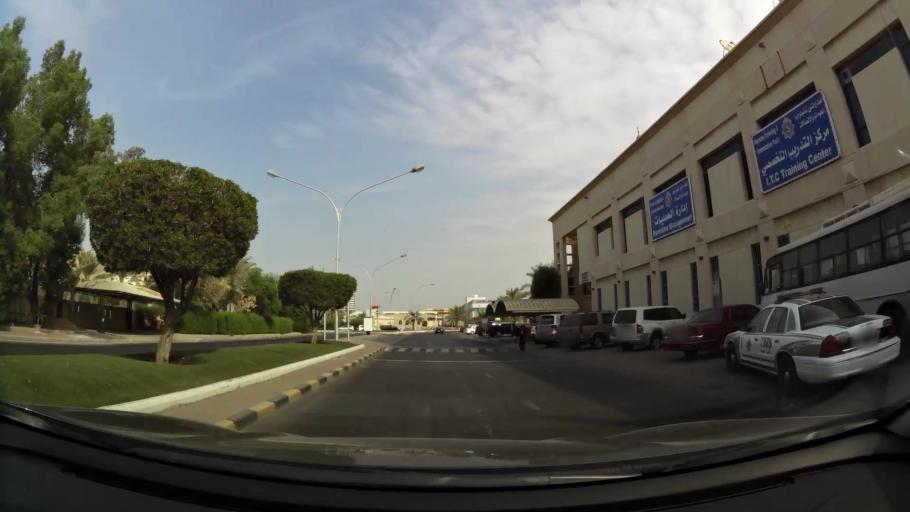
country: KW
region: Al Farwaniyah
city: Al Farwaniyah
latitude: 29.3109
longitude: 47.9685
